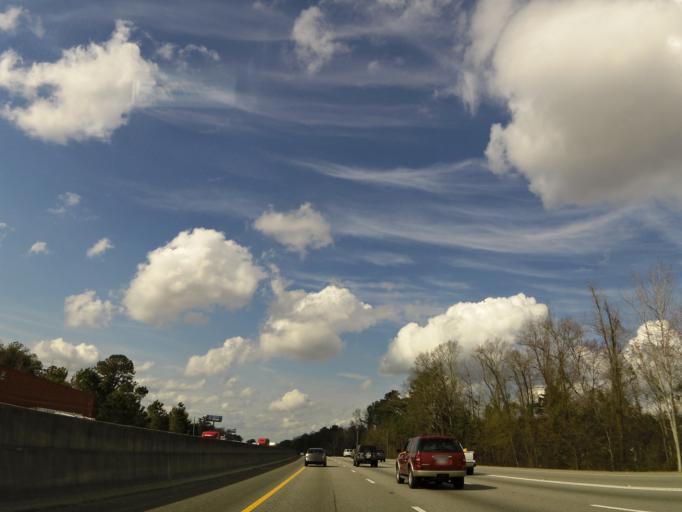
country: US
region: South Carolina
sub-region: Berkeley County
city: Hanahan
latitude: 32.9427
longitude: -80.0522
